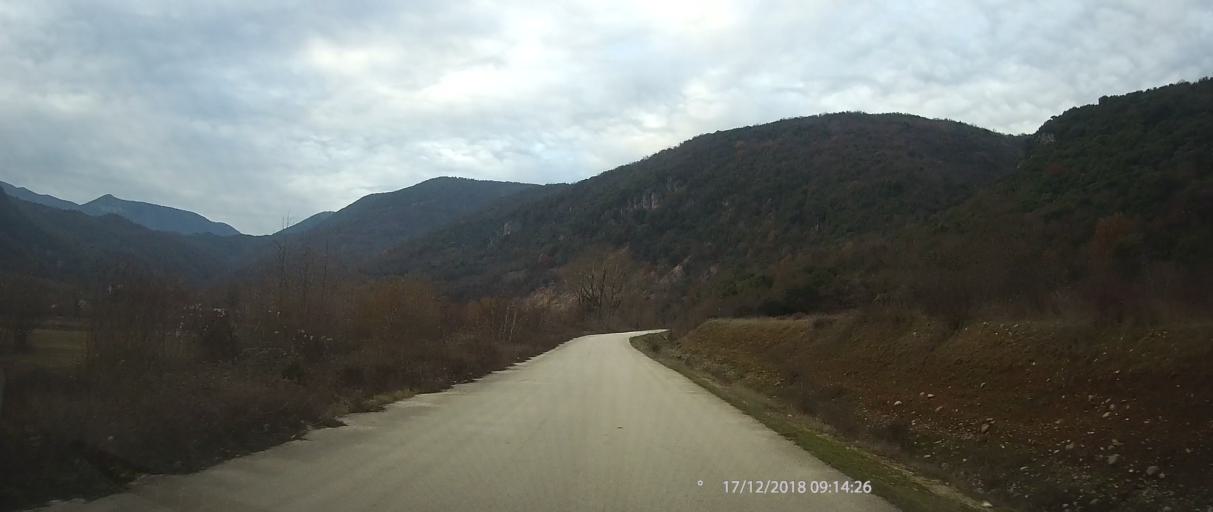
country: GR
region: Epirus
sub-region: Nomos Ioanninon
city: Kalpaki
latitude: 39.9736
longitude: 20.6560
